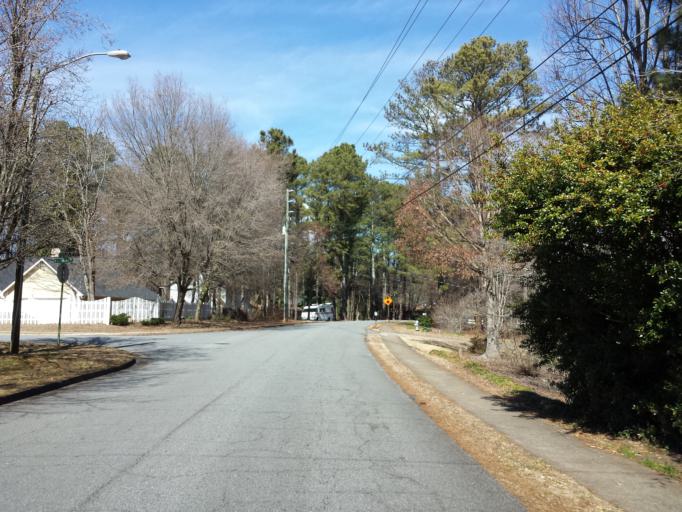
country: US
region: Georgia
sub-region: Cobb County
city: Smyrna
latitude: 33.9384
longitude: -84.4739
